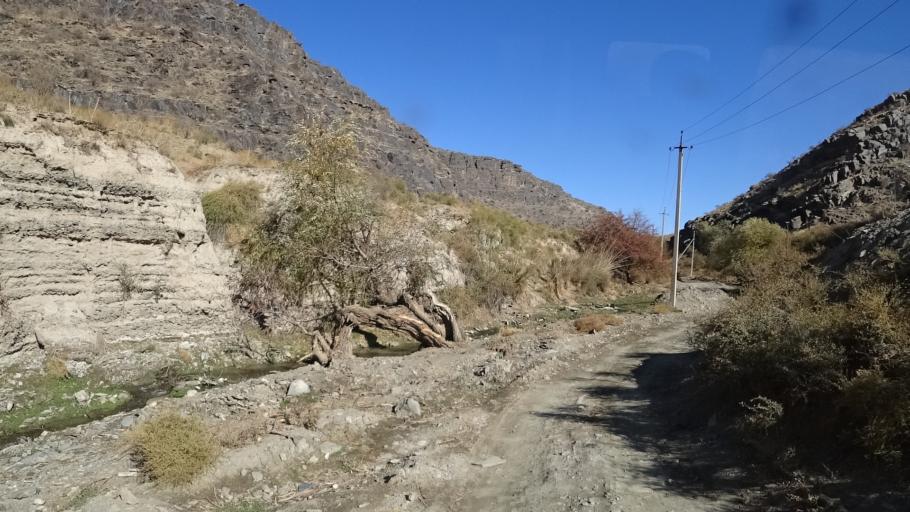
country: UZ
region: Navoiy
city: Nurota
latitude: 40.3086
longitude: 65.6201
